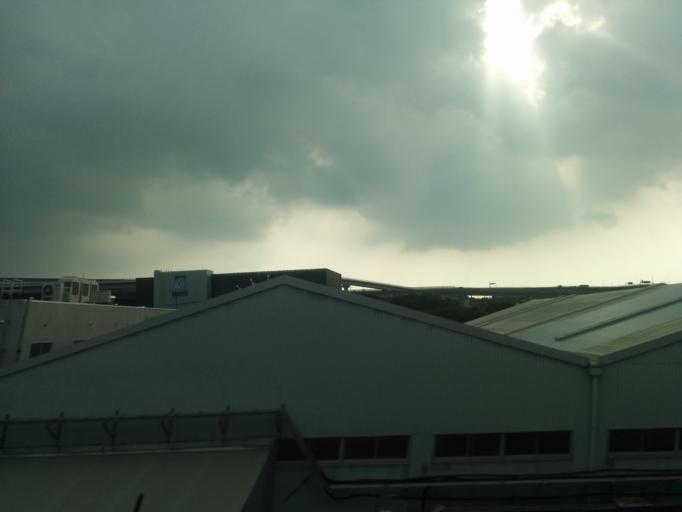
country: JP
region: Aichi
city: Obu
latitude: 35.0497
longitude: 136.9525
